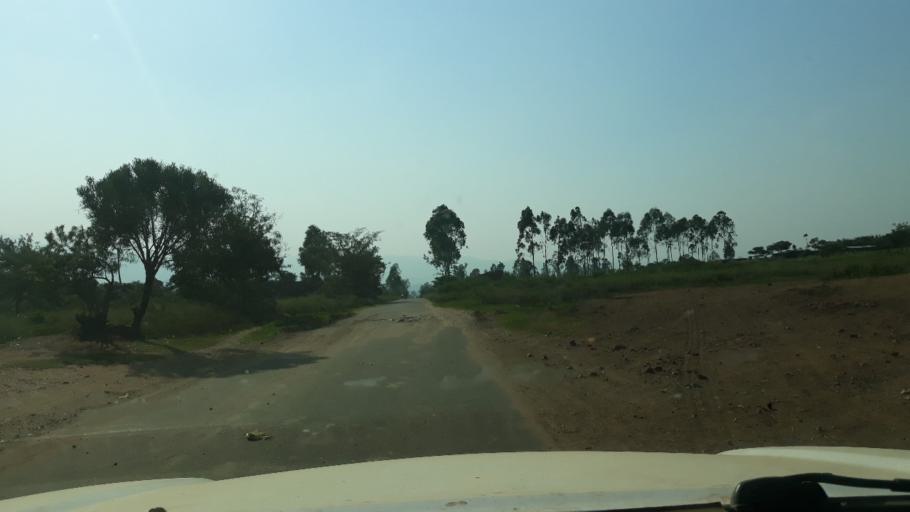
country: BI
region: Cibitoke
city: Cibitoke
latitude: -2.8470
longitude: 29.0228
